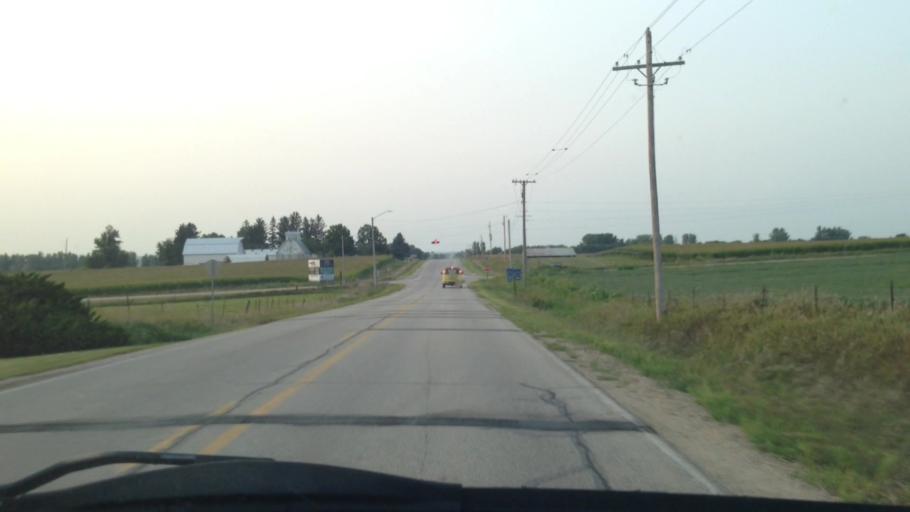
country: US
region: Iowa
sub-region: Benton County
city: Atkins
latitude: 41.9912
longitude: -91.8732
